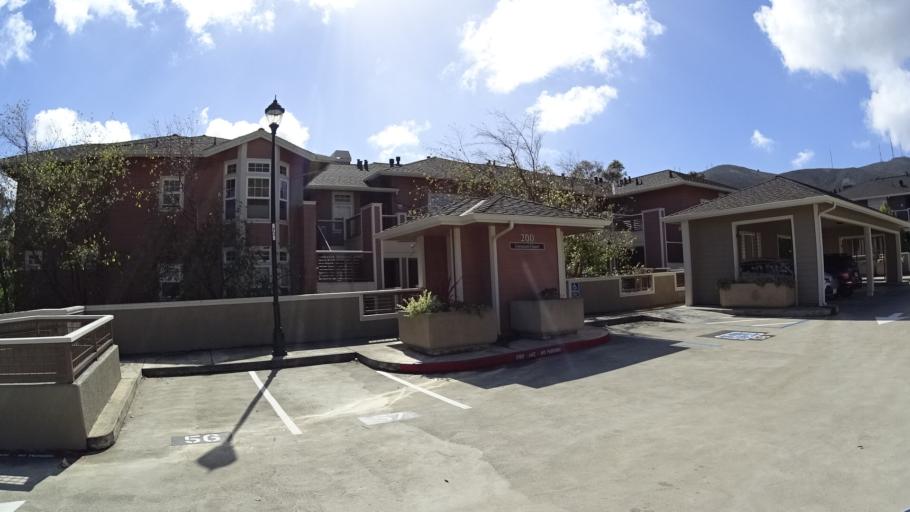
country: US
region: California
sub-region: San Mateo County
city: Brisbane
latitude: 37.6927
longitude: -122.4164
